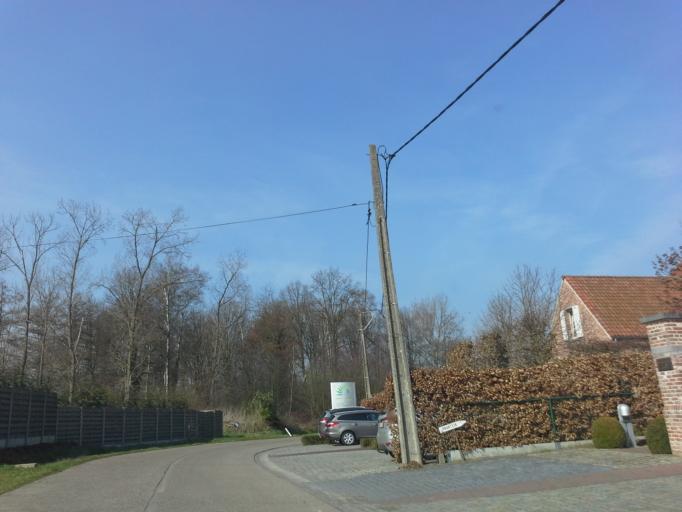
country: BE
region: Flanders
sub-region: Provincie Antwerpen
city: Meerhout
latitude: 51.1237
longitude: 5.0486
